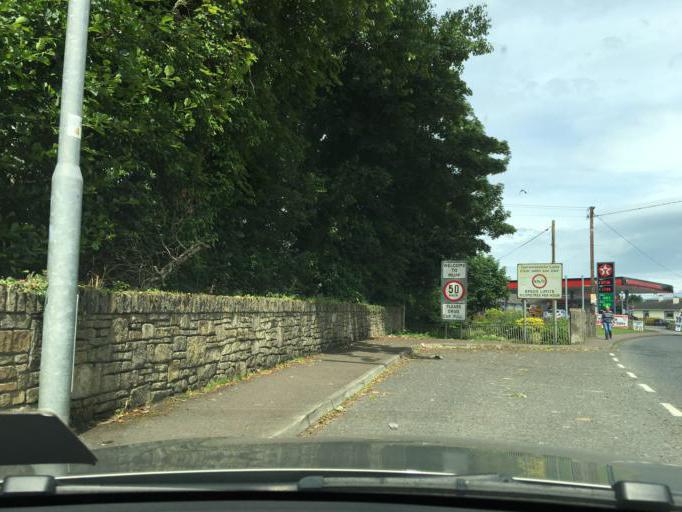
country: IE
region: Ulster
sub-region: County Donegal
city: Muff
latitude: 55.0647
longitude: -7.2700
